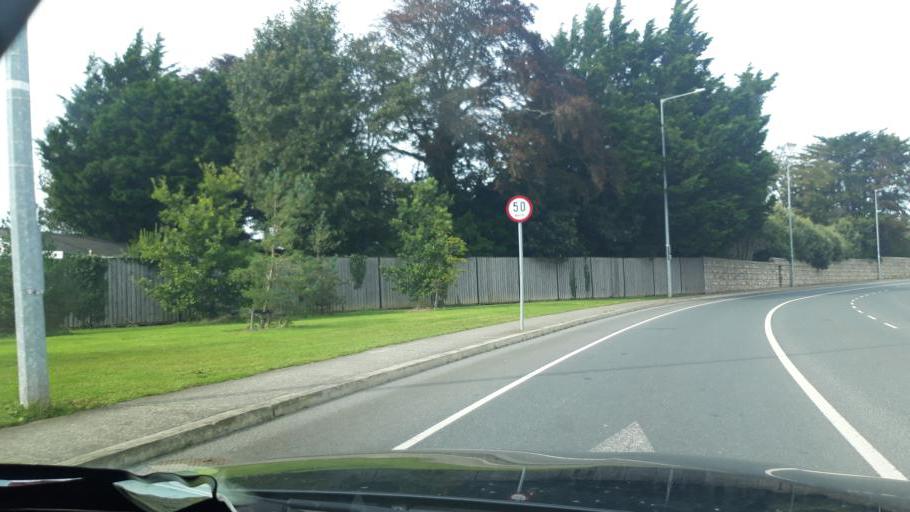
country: IE
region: Leinster
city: Sandyford
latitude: 53.2629
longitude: -6.2108
